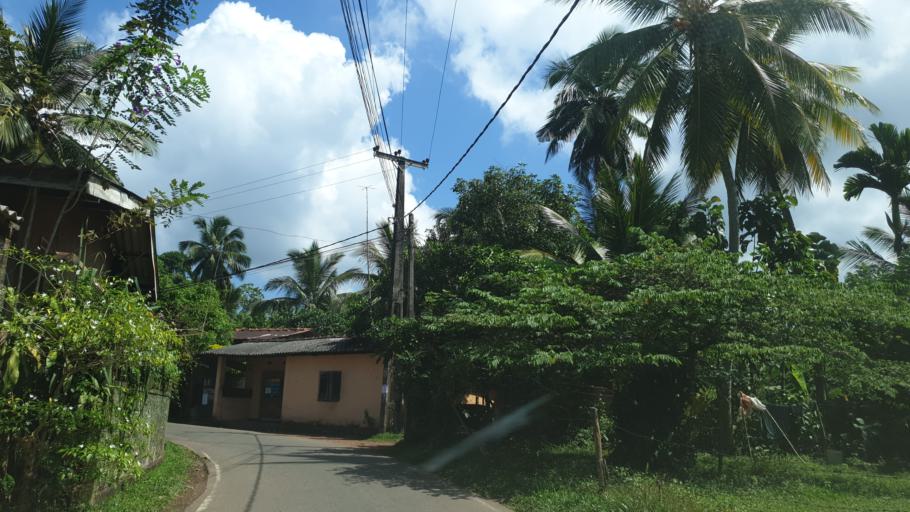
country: LK
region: Western
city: Panadura
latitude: 6.6743
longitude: 79.9393
